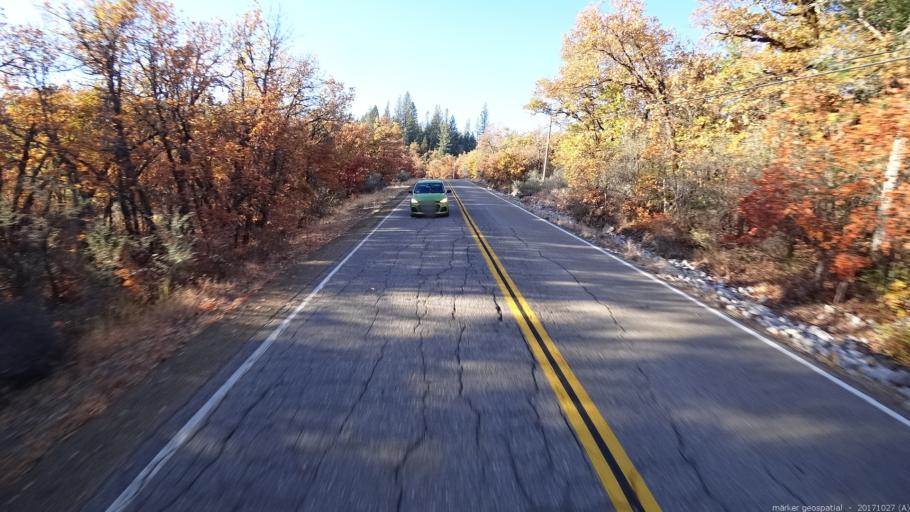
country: US
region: California
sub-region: Shasta County
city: Burney
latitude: 41.0067
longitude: -121.9142
